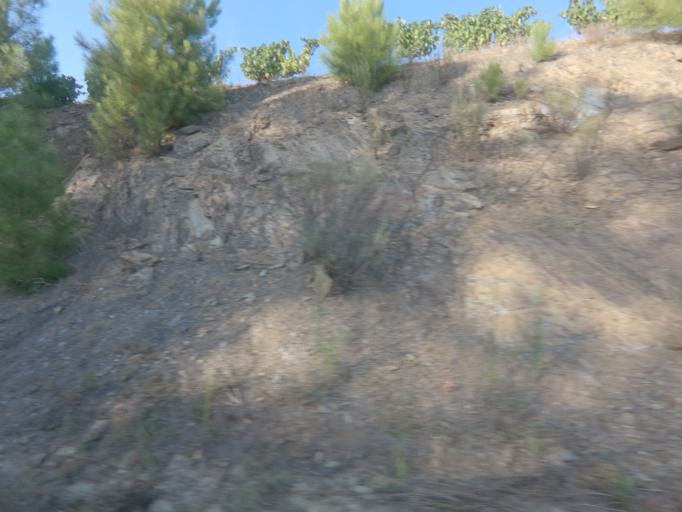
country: PT
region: Vila Real
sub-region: Sabrosa
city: Sabrosa
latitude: 41.2668
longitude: -7.5463
